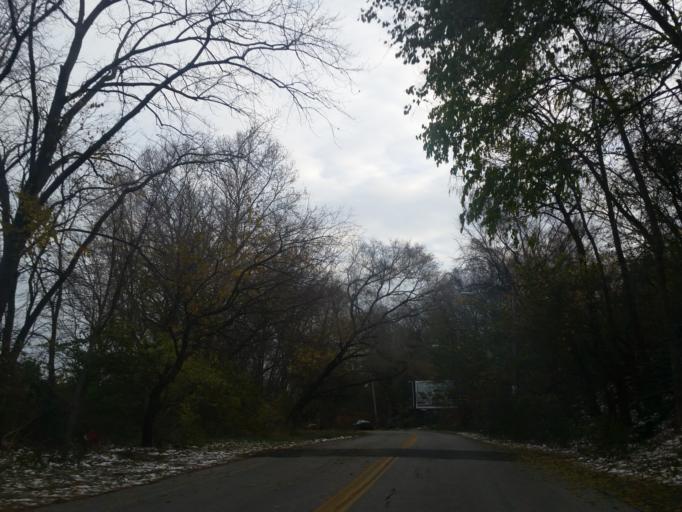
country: US
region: Ohio
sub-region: Cuyahoga County
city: Cleveland
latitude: 41.4758
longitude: -81.7051
